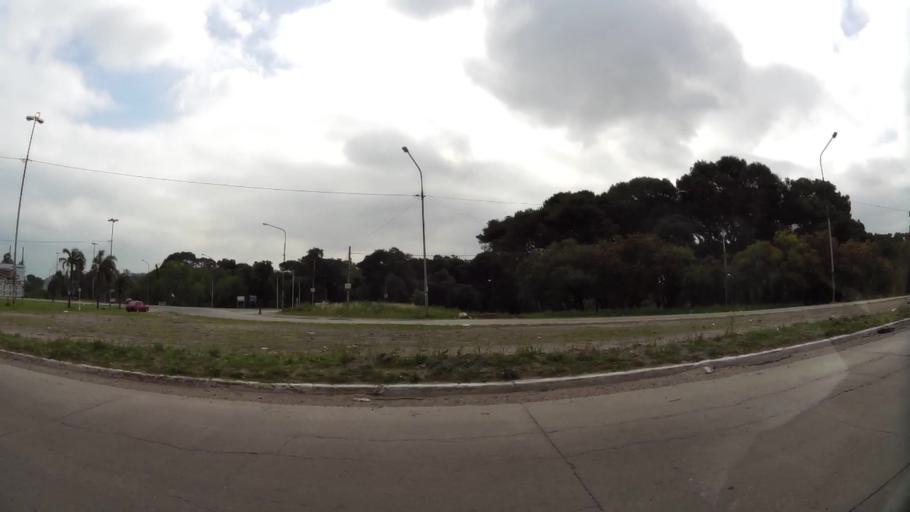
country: AR
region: Buenos Aires
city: San Justo
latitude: -34.7218
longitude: -58.5355
